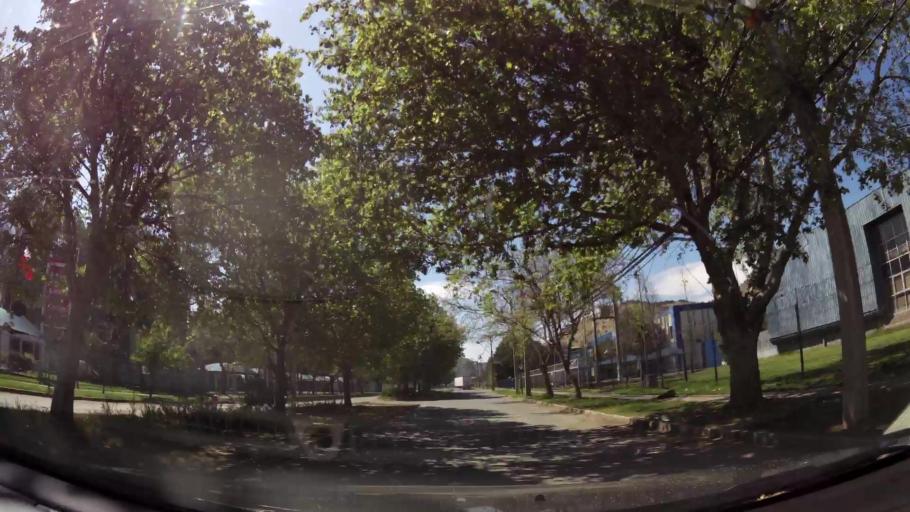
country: CL
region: Santiago Metropolitan
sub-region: Provincia de Santiago
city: Lo Prado
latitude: -33.3812
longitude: -70.7447
